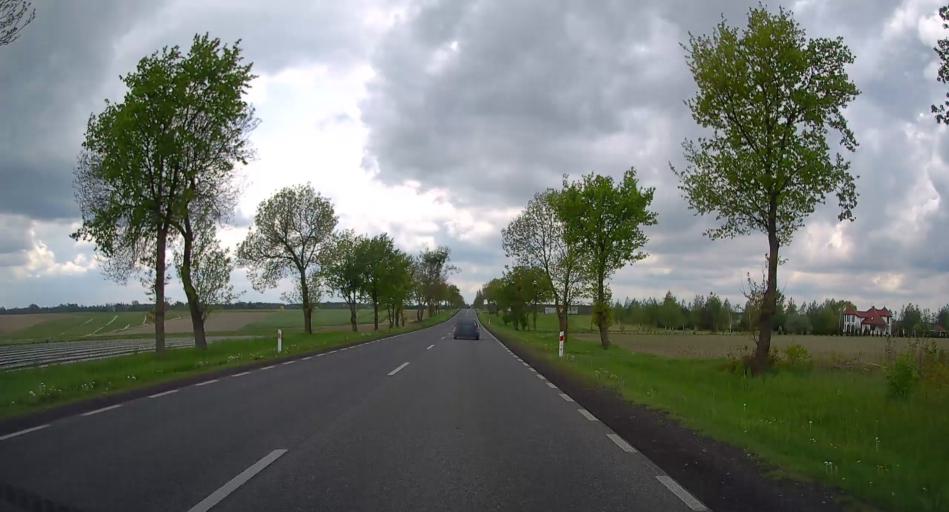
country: PL
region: Masovian Voivodeship
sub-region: Powiat plonski
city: Zaluski
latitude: 52.4389
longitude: 20.4812
